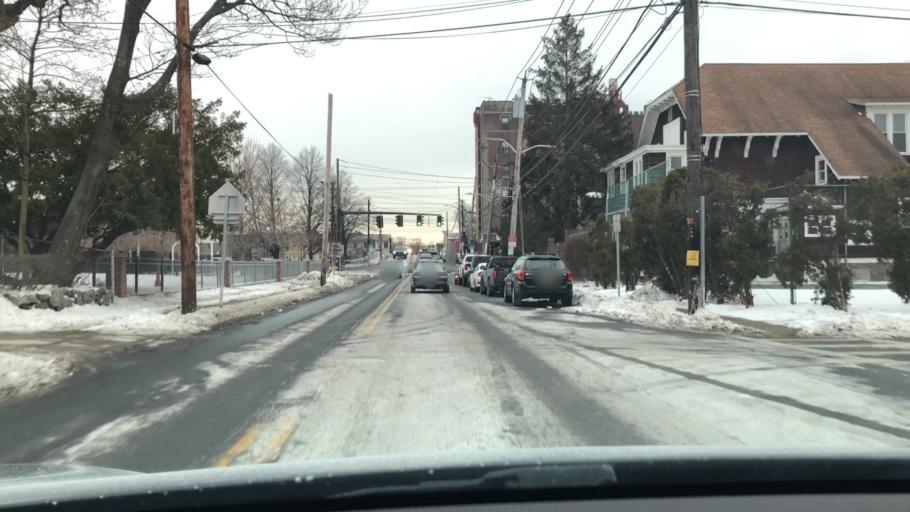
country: US
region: New York
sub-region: Westchester County
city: Harrison
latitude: 40.9708
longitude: -73.7132
